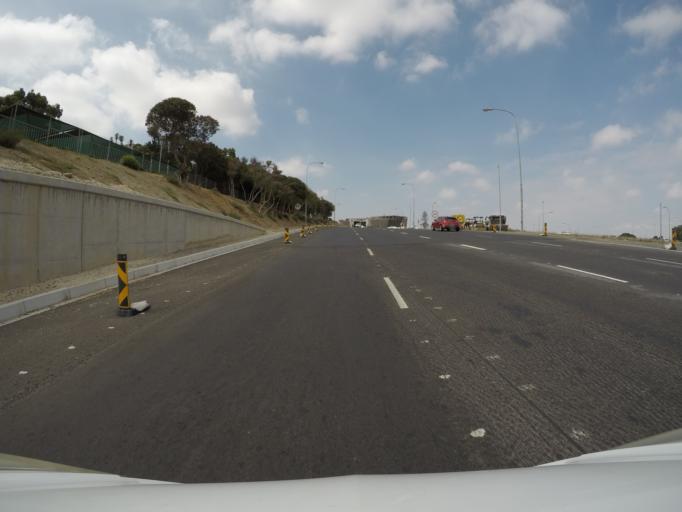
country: ZA
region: Western Cape
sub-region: City of Cape Town
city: Kraaifontein
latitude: -33.8868
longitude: 18.6330
